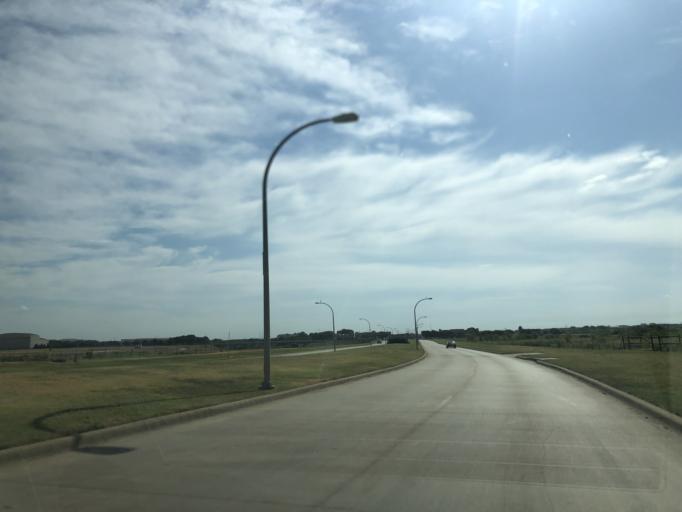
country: US
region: Texas
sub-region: Tarrant County
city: Haslet
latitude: 32.9723
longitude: -97.3191
